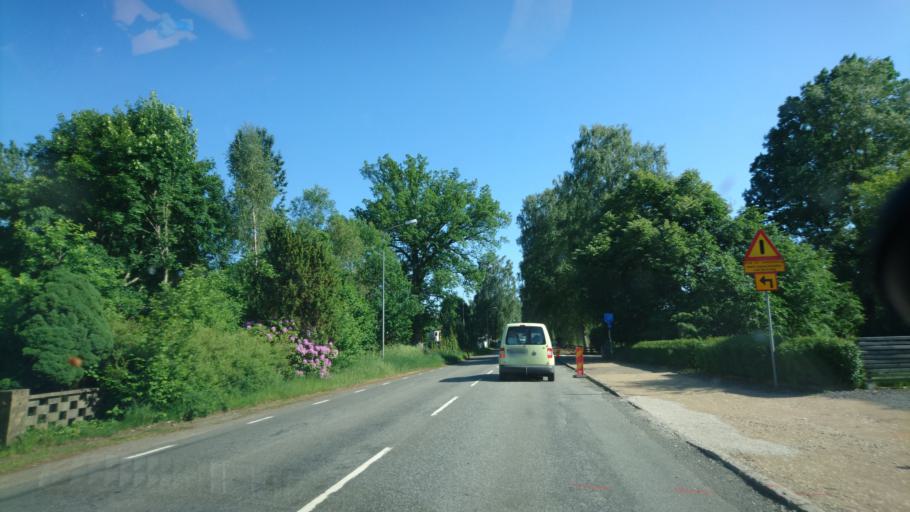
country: SE
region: Skane
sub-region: Osby Kommun
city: Lonsboda
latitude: 56.4054
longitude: 14.3178
